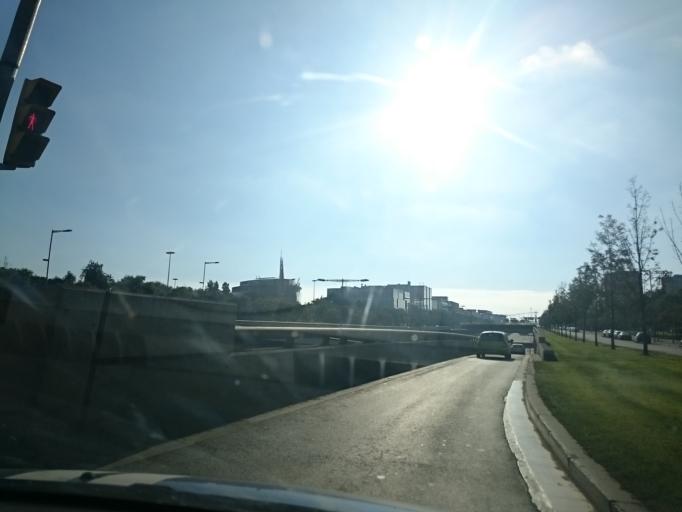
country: ES
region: Catalonia
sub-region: Provincia de Barcelona
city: L'Hospitalet de Llobregat
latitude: 41.3543
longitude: 2.1214
